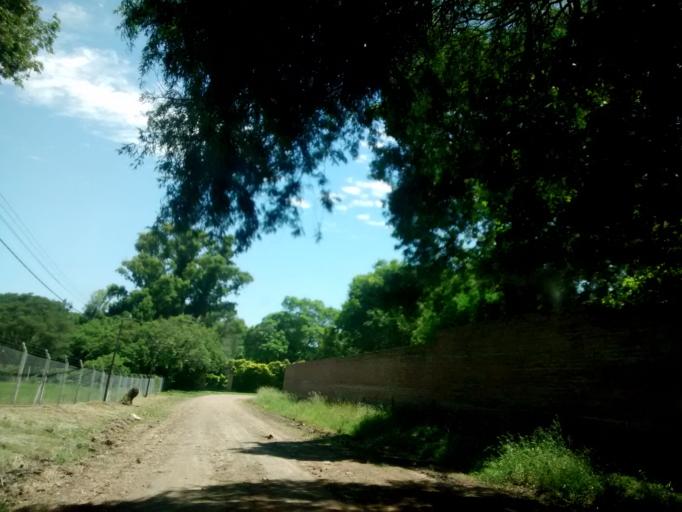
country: AR
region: Chaco
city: Resistencia
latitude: -27.4186
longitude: -58.9645
